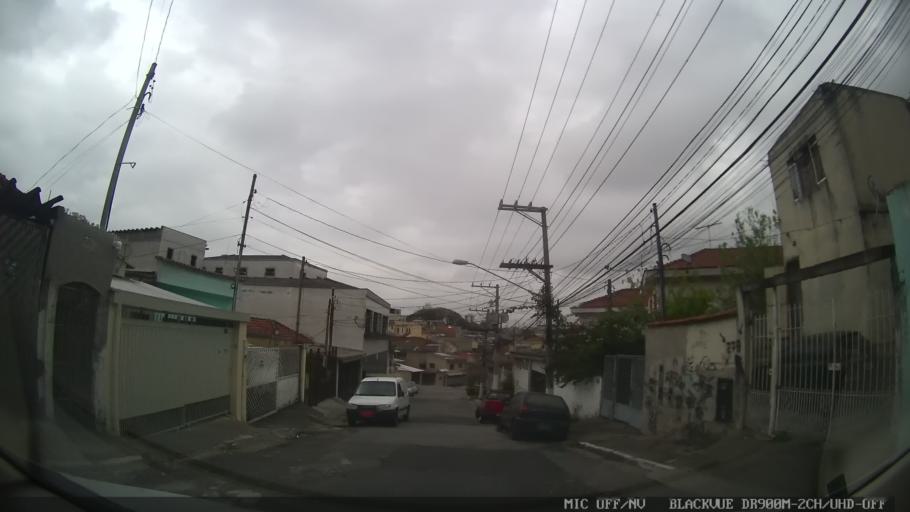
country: BR
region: Sao Paulo
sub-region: Sao Paulo
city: Sao Paulo
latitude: -23.4941
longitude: -46.5999
